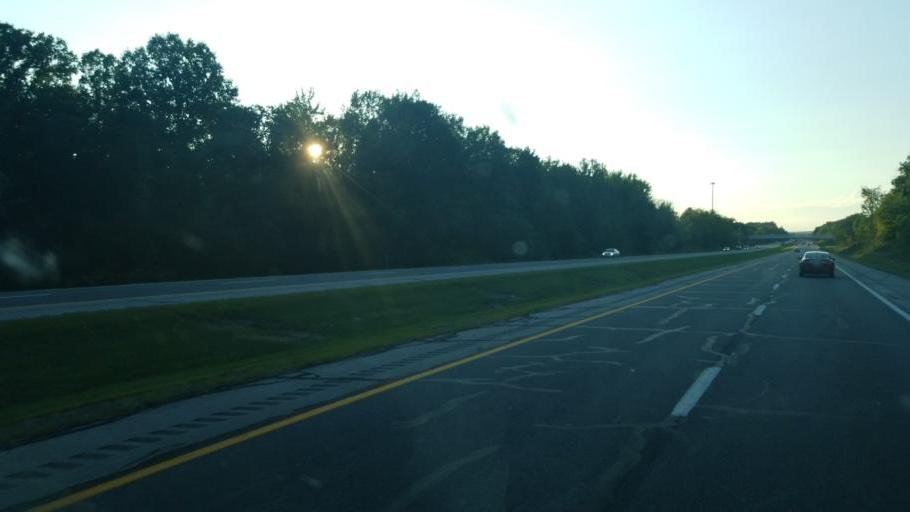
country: US
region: Ohio
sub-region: Mahoning County
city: Canfield
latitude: 41.0521
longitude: -80.7719
